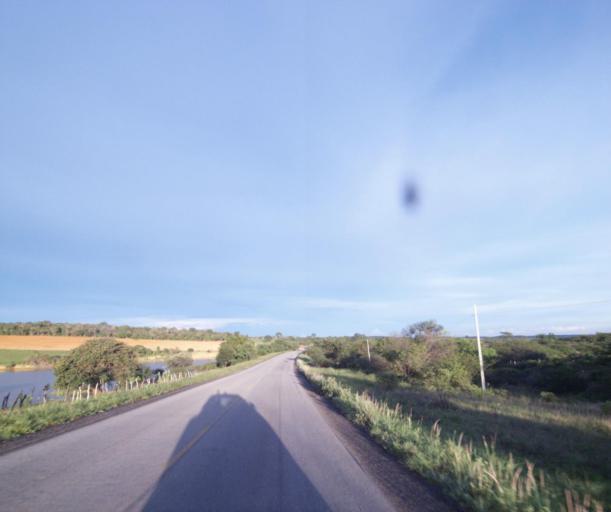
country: BR
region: Bahia
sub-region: Brumado
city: Brumado
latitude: -14.2279
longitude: -41.9292
